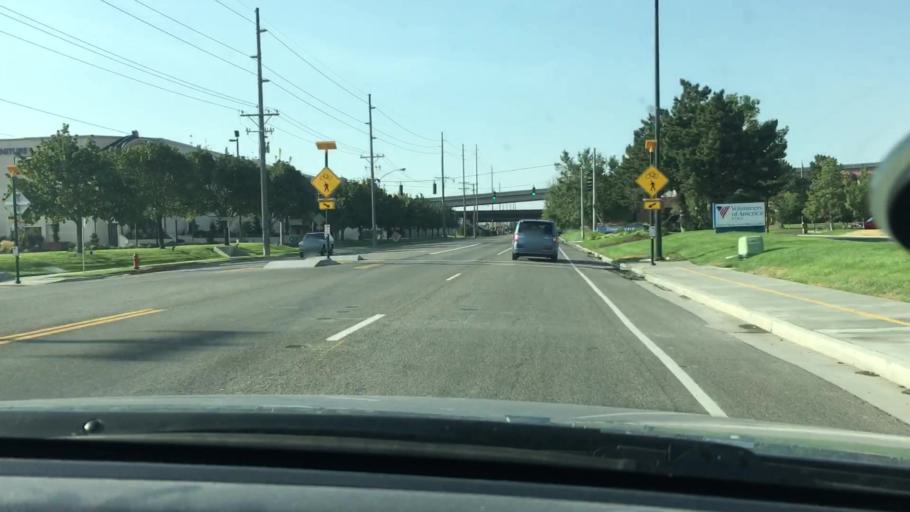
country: US
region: Utah
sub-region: Salt Lake County
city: South Salt Lake
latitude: 40.7215
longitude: -111.8998
